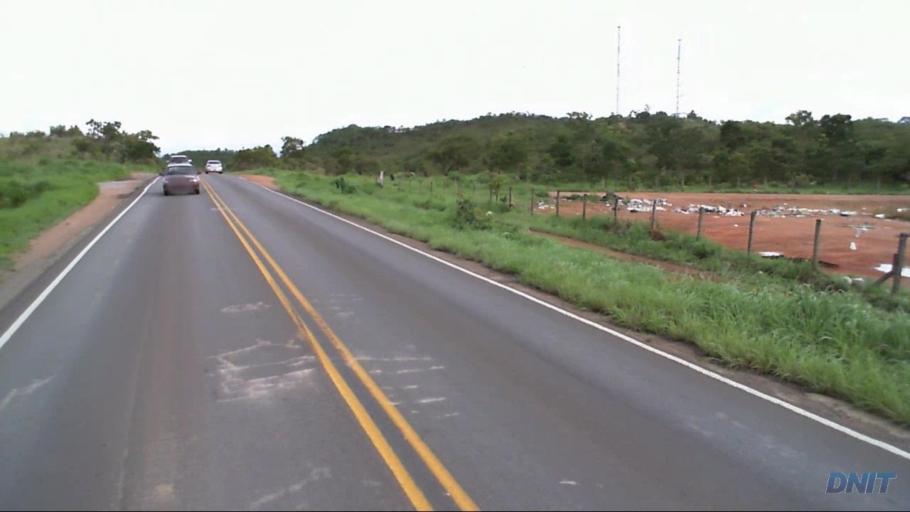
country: BR
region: Goias
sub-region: Padre Bernardo
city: Padre Bernardo
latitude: -15.2256
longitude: -48.2783
